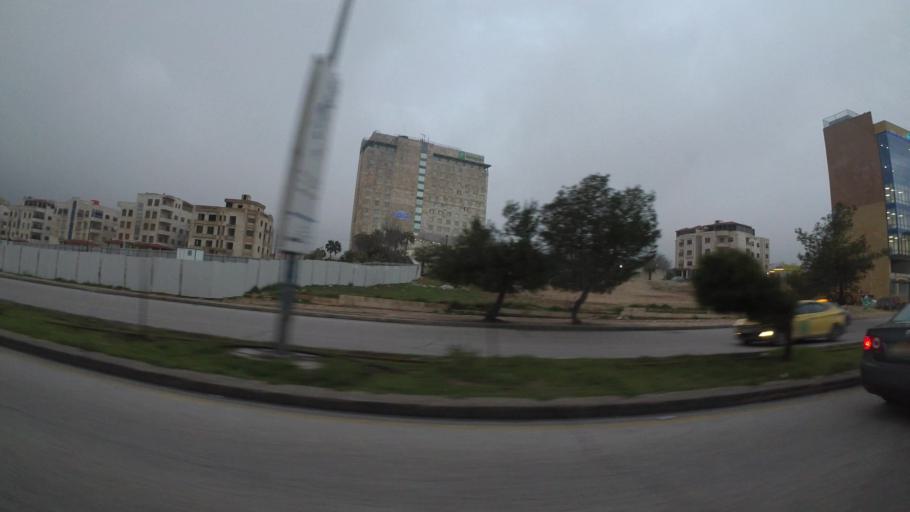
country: JO
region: Amman
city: Al Jubayhah
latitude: 31.9858
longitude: 35.8663
